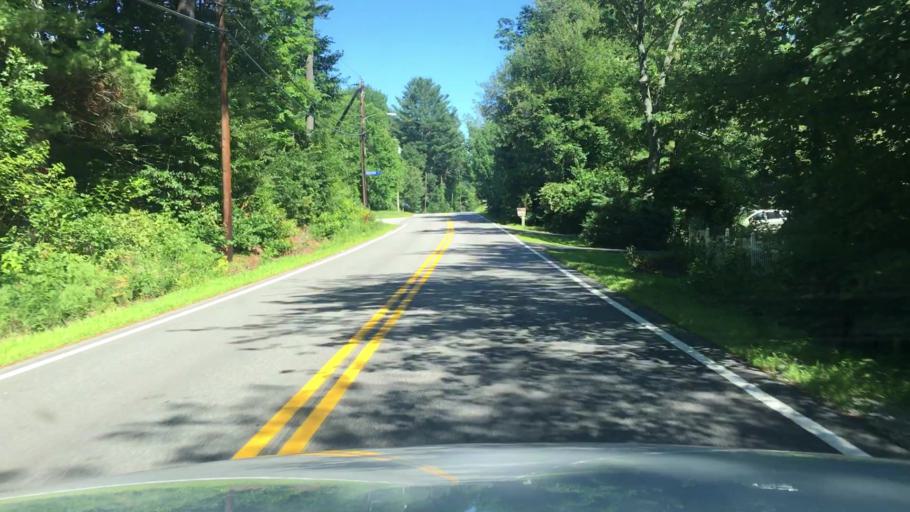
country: US
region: New Hampshire
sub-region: Merrimack County
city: South Hooksett
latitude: 43.0404
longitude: -71.4170
